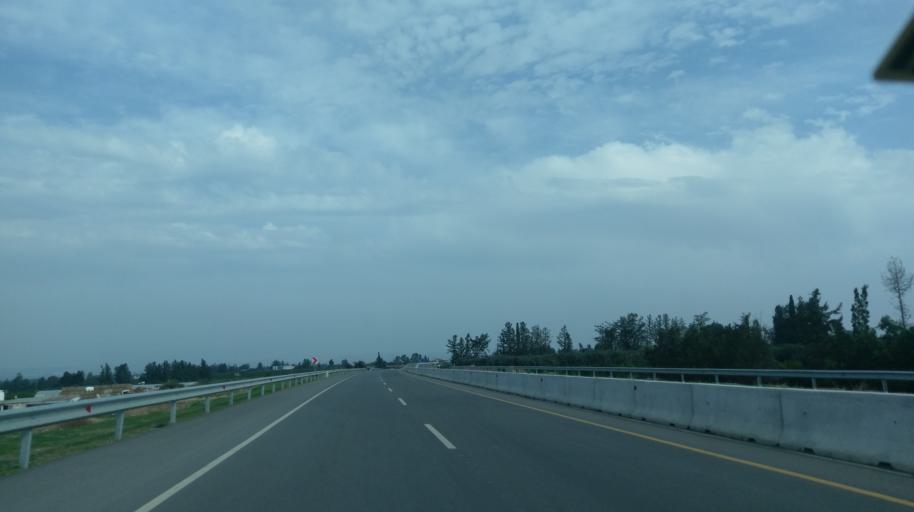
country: CY
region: Lefkosia
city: Morfou
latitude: 35.1690
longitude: 32.9440
